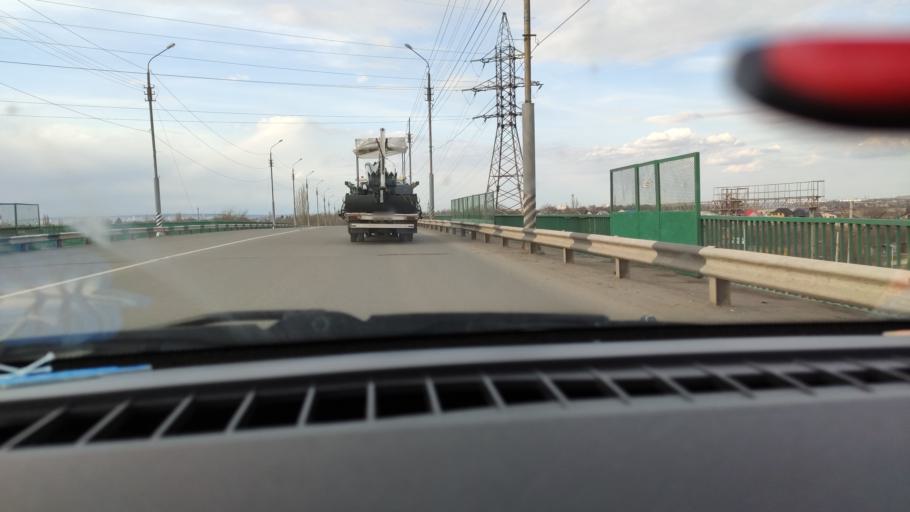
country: RU
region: Saratov
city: Privolzhskiy
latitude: 51.4184
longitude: 46.0465
